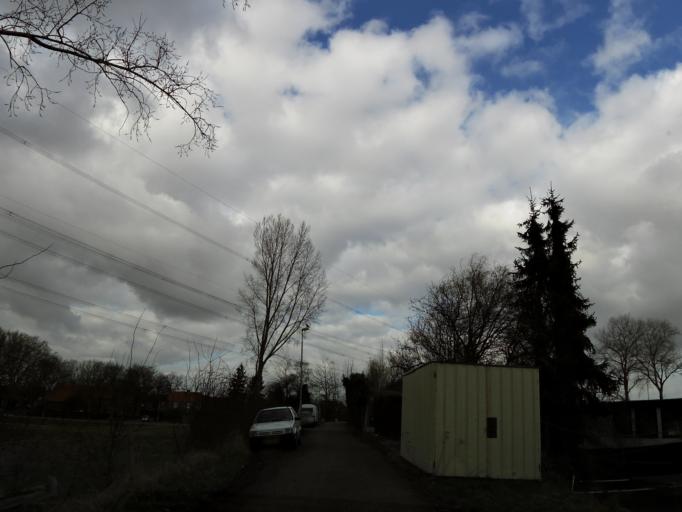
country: NL
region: Limburg
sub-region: Gemeente Sittard-Geleen
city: Born
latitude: 51.0445
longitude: 5.7927
